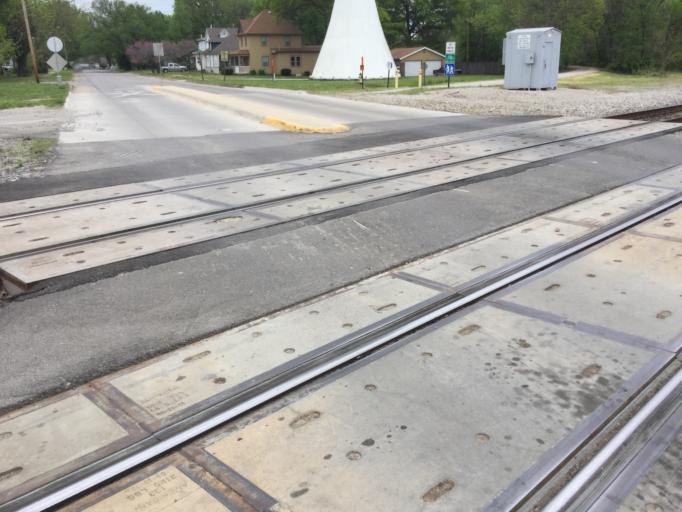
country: US
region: Kansas
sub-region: Labette County
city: Parsons
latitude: 37.3346
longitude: -95.2633
